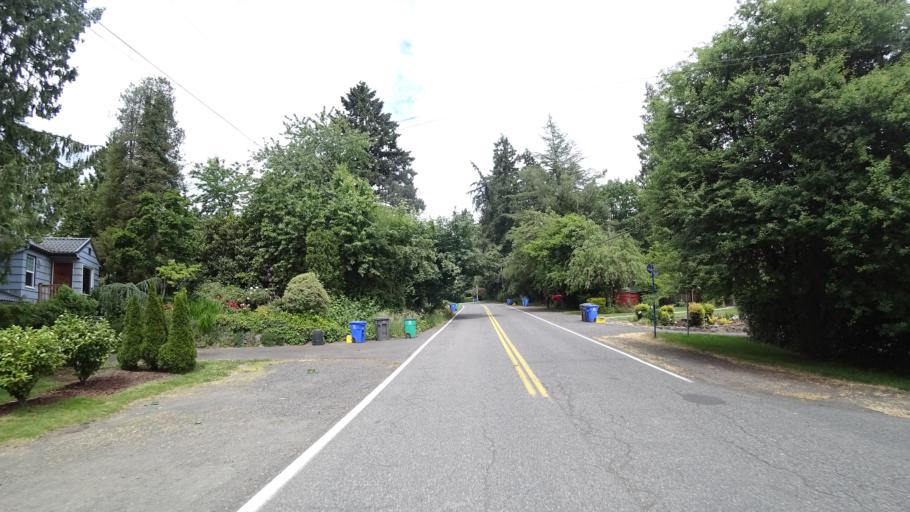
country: US
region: Oregon
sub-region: Clackamas County
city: Lake Oswego
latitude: 45.4597
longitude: -122.6924
